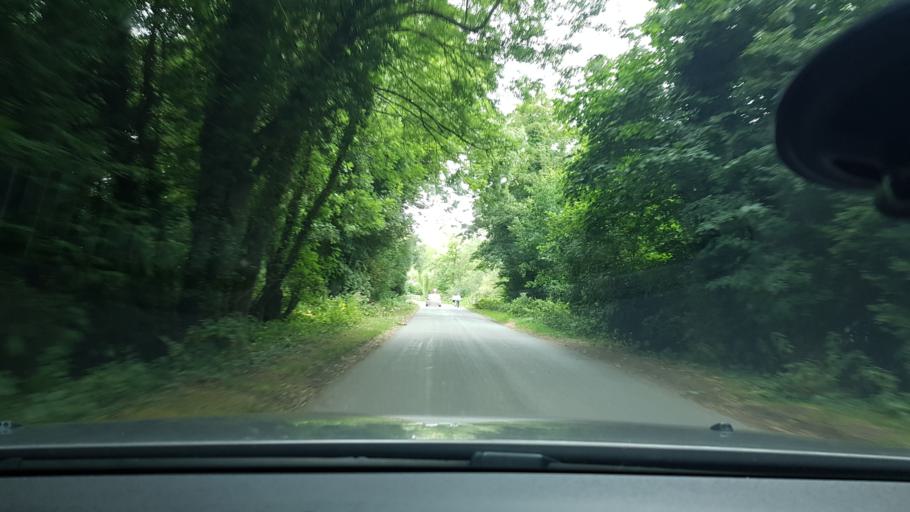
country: GB
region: England
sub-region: Wiltshire
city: Ramsbury
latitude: 51.4408
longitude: -1.6011
